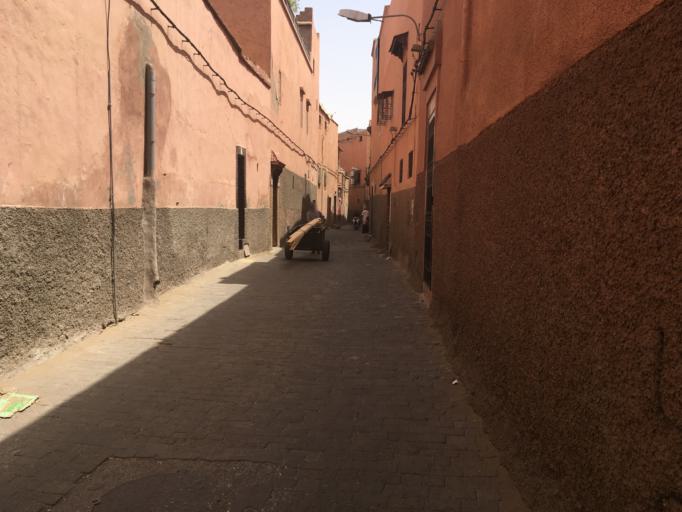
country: MA
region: Marrakech-Tensift-Al Haouz
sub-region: Marrakech
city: Marrakesh
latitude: 31.6241
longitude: -7.9848
